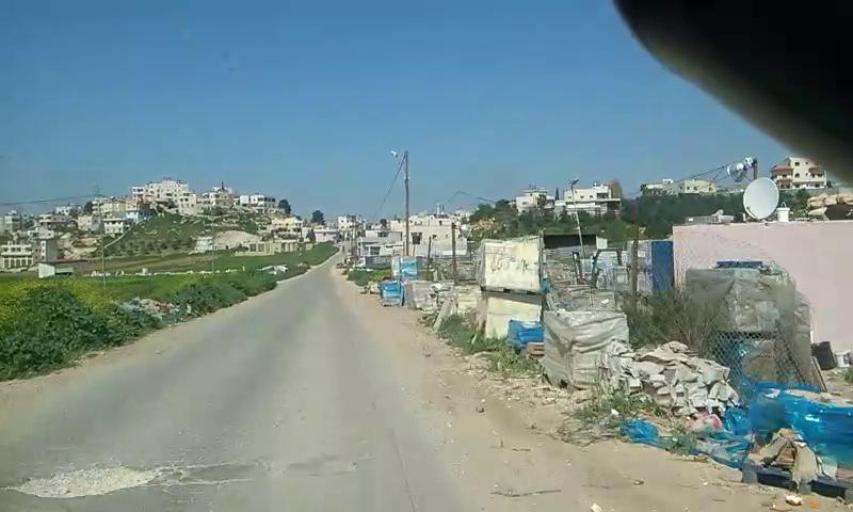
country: PS
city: Dayr Samit
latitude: 31.5148
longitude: 34.9707
